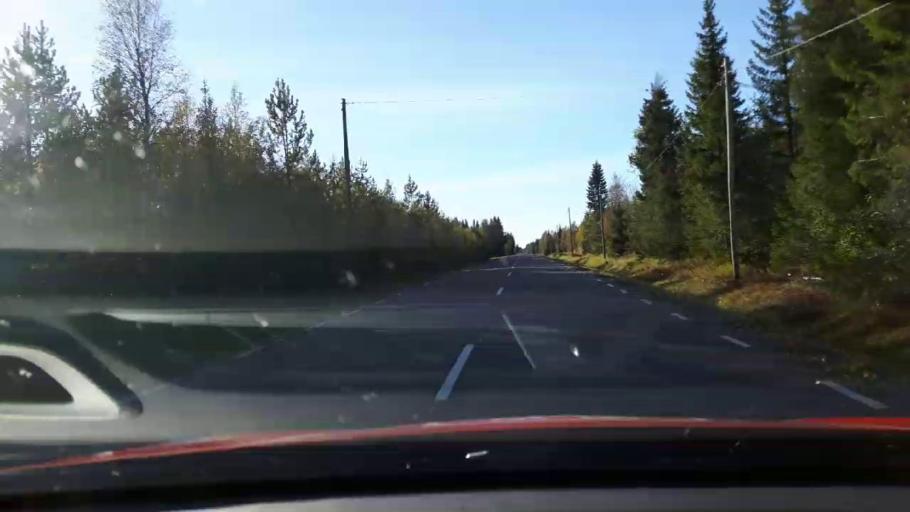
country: SE
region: Jaemtland
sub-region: Stroemsunds Kommun
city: Stroemsund
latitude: 63.8591
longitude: 15.1920
